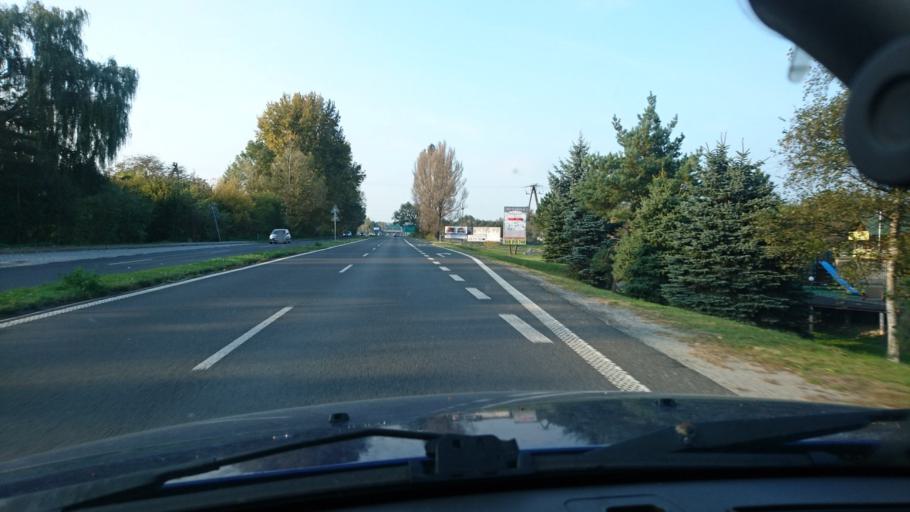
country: PL
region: Silesian Voivodeship
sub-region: Powiat cieszynski
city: Gorki Wielkie
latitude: 49.7792
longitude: 18.8082
